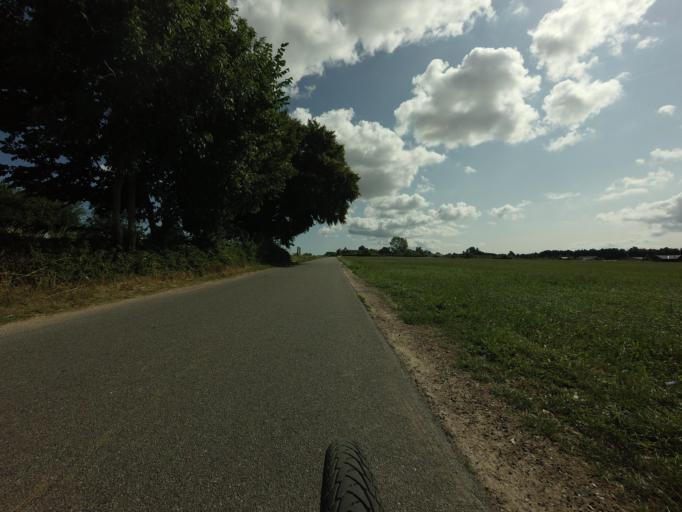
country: DK
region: Zealand
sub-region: Vordingborg Kommune
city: Stege
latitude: 54.9731
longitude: 12.3815
